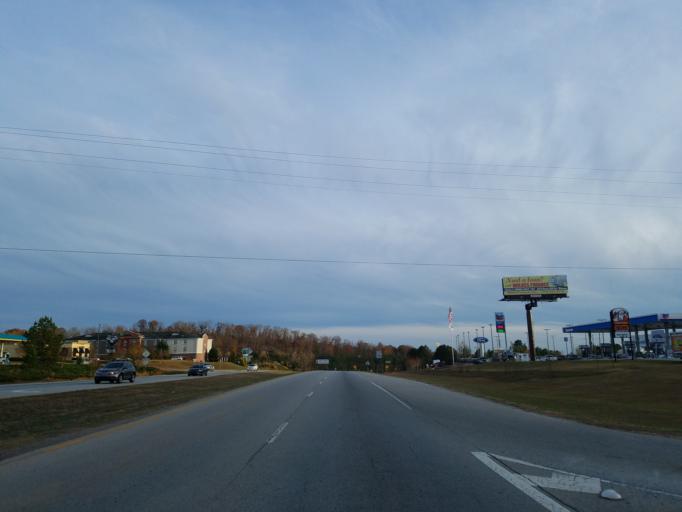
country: US
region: Georgia
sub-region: Haralson County
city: Bremen
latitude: 33.6938
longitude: -85.1540
